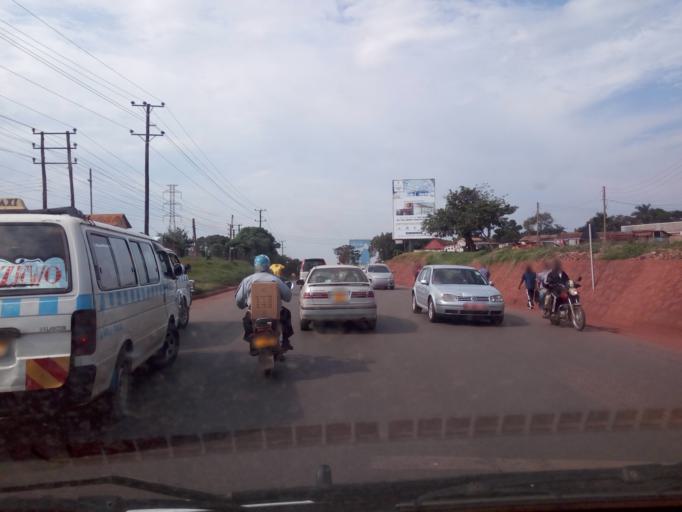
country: UG
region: Central Region
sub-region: Kampala District
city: Kampala
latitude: 0.3312
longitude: 32.6150
